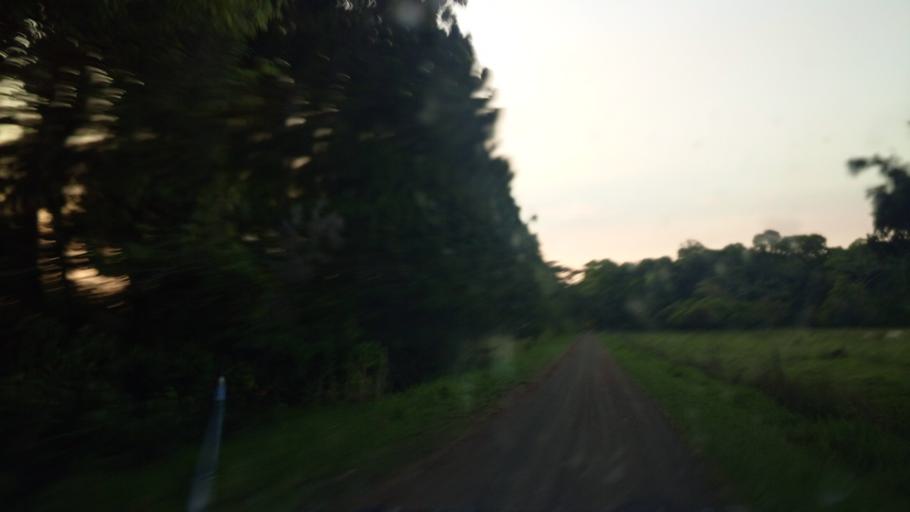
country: AU
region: Queensland
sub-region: Tablelands
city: Atherton
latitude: -17.3664
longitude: 145.7516
